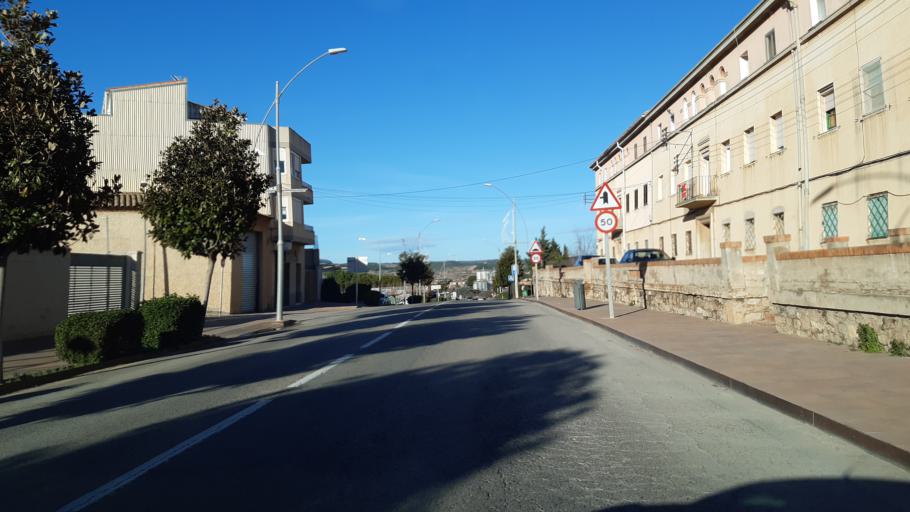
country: ES
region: Catalonia
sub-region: Provincia de Tarragona
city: Gandesa
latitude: 41.0567
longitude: 0.4411
